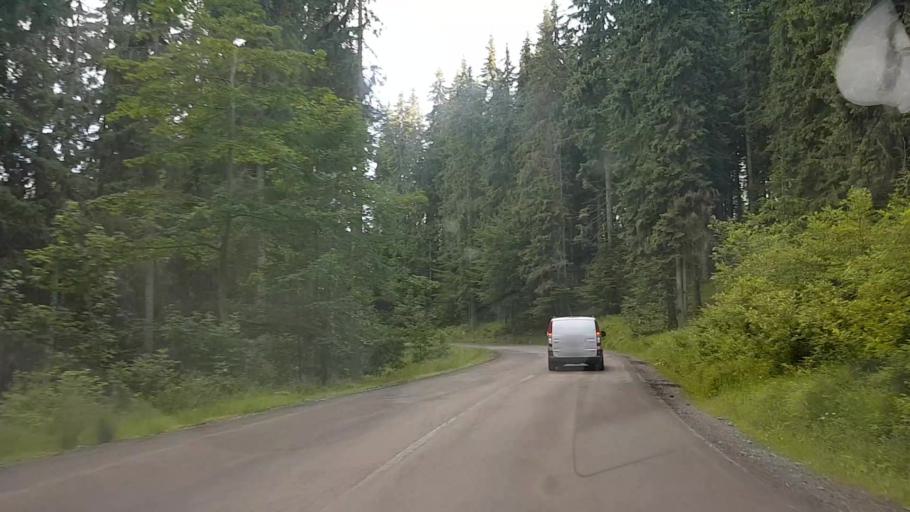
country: RO
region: Harghita
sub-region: Comuna Varsag
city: Varsag
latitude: 46.6659
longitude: 25.3057
